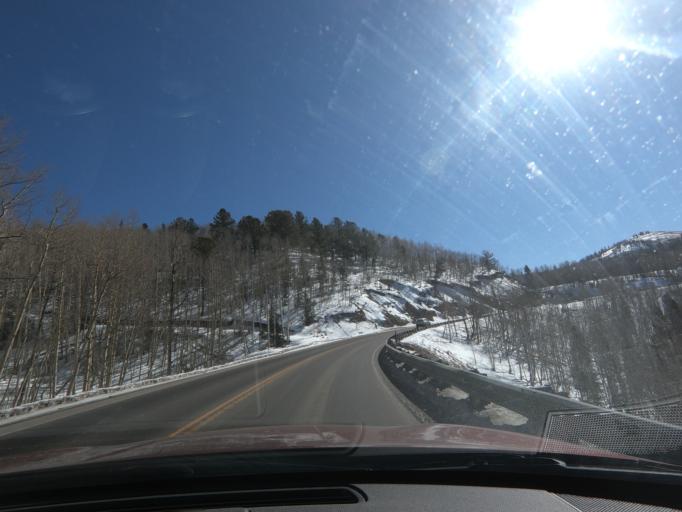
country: US
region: Colorado
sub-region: Teller County
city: Cripple Creek
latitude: 38.8022
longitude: -105.1196
